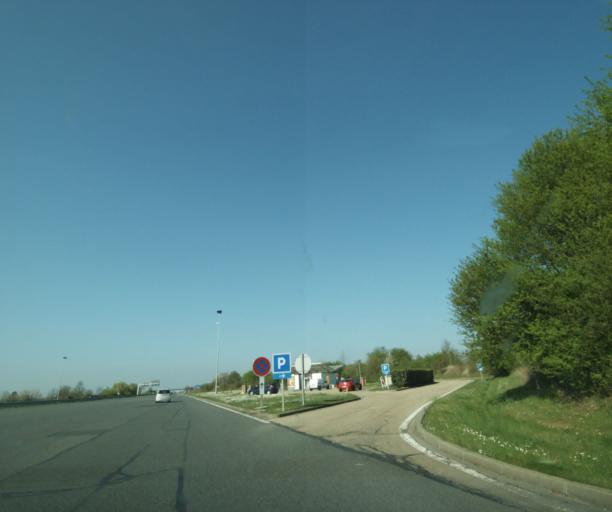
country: FR
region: Ile-de-France
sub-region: Departement de Seine-et-Marne
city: Souppes-sur-Loing
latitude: 48.1767
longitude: 2.7673
